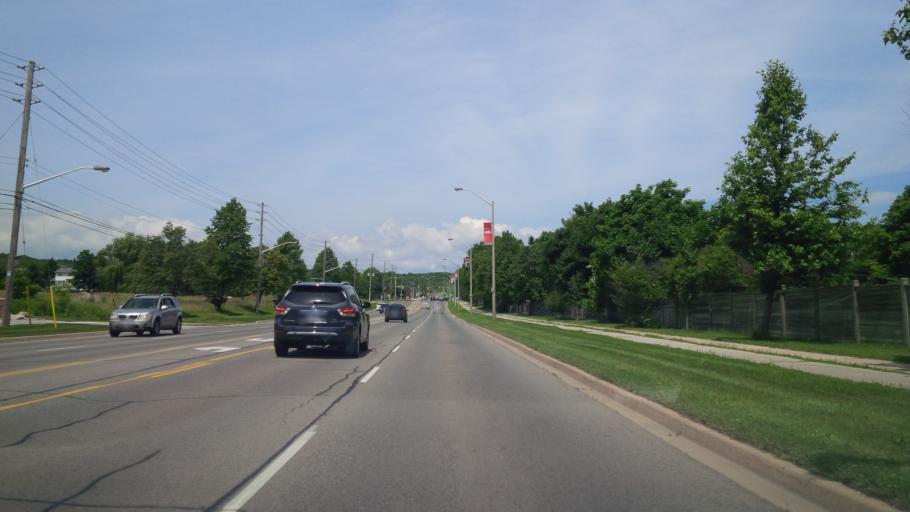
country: CA
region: Ontario
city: Burlington
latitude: 43.3532
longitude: -79.8383
